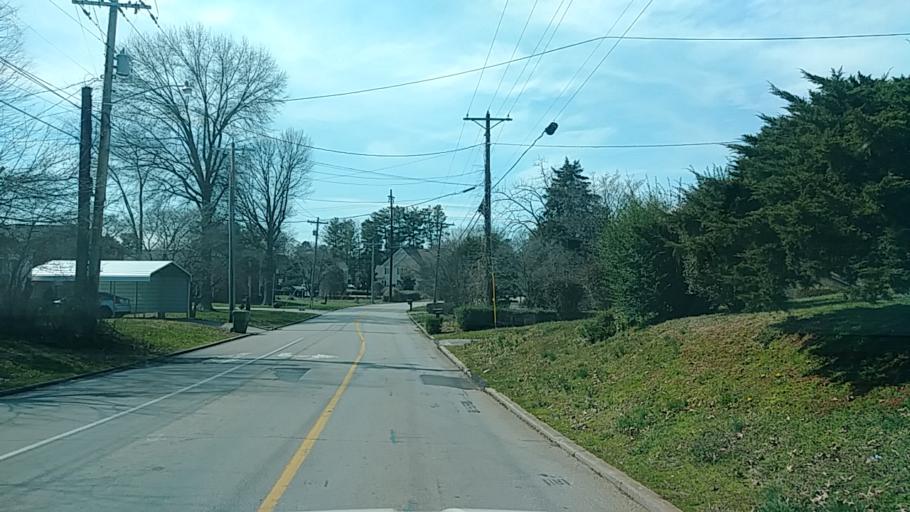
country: US
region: Tennessee
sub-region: Hamblen County
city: Morristown
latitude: 36.2110
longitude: -83.3200
